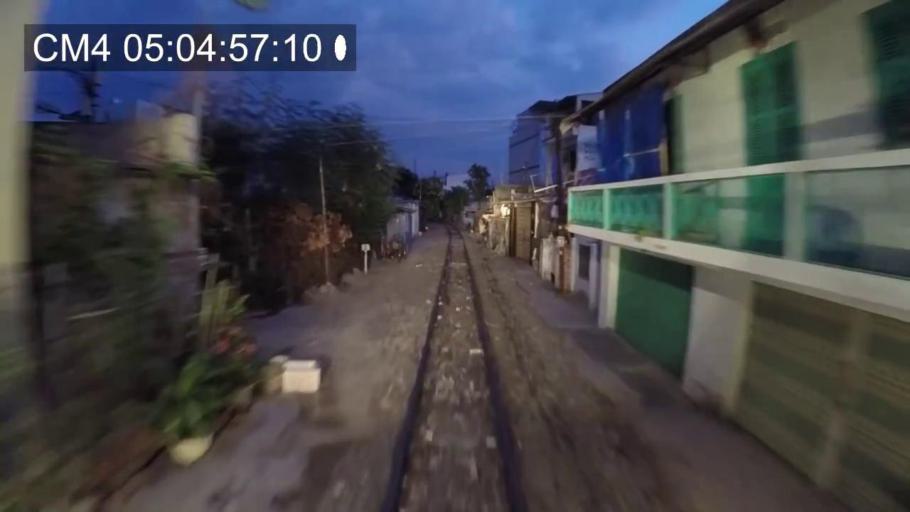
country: VN
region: Khanh Hoa
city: Nha Trang
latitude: 12.2677
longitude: 109.1737
